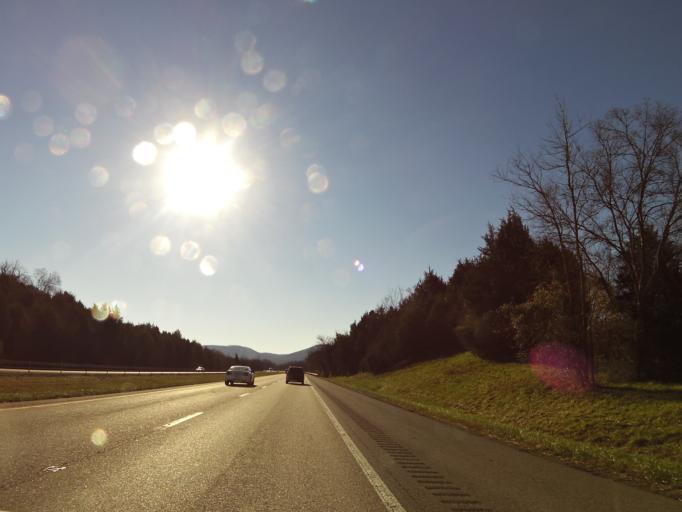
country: US
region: Tennessee
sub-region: Cocke County
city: Newport
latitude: 35.9937
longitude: -83.2861
